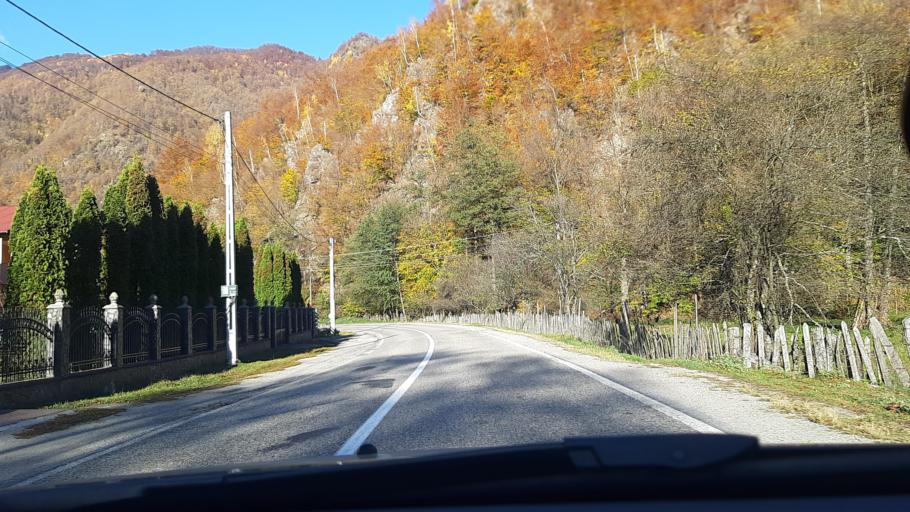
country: RO
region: Valcea
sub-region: Comuna Malaia
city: Malaia
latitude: 45.3551
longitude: 24.1218
